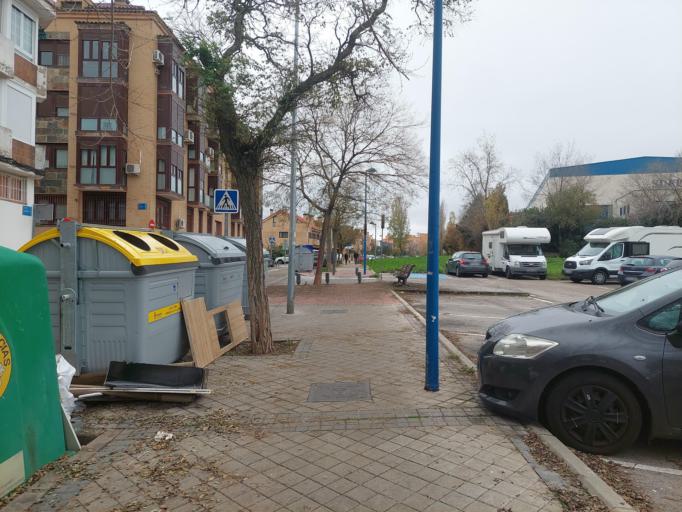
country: ES
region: Madrid
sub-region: Provincia de Madrid
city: Leganes
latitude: 40.3209
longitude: -3.7570
